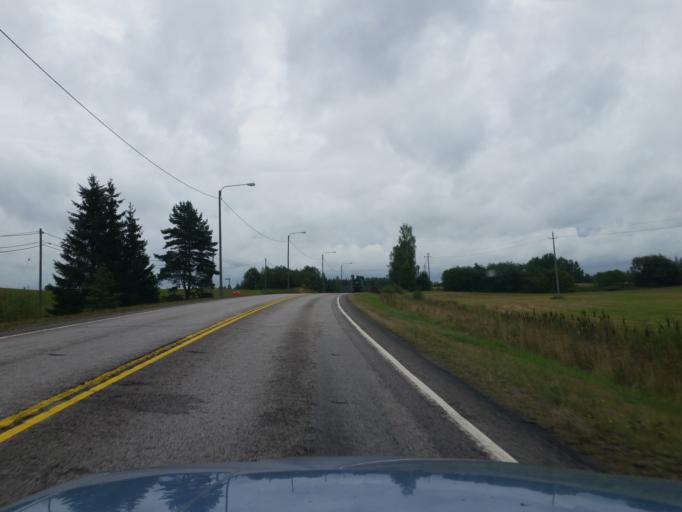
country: FI
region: Uusimaa
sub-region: Helsinki
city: Lohja
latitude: 60.3706
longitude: 24.1465
